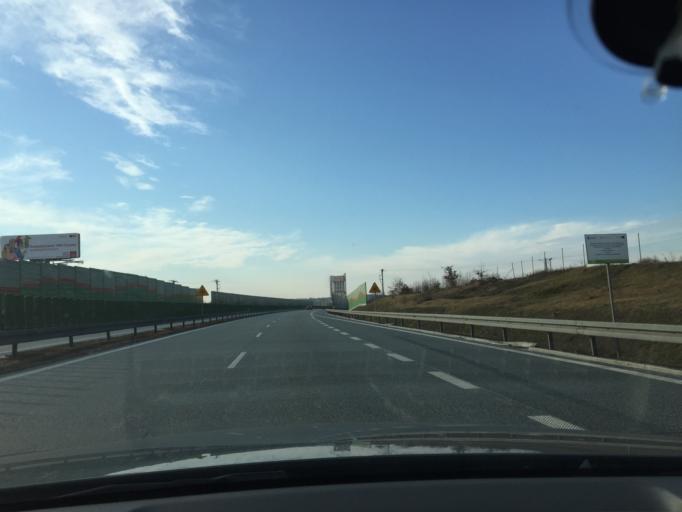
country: PL
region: Lodz Voivodeship
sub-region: Powiat rawski
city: Rawa Mazowiecka
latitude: 51.7693
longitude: 20.2726
